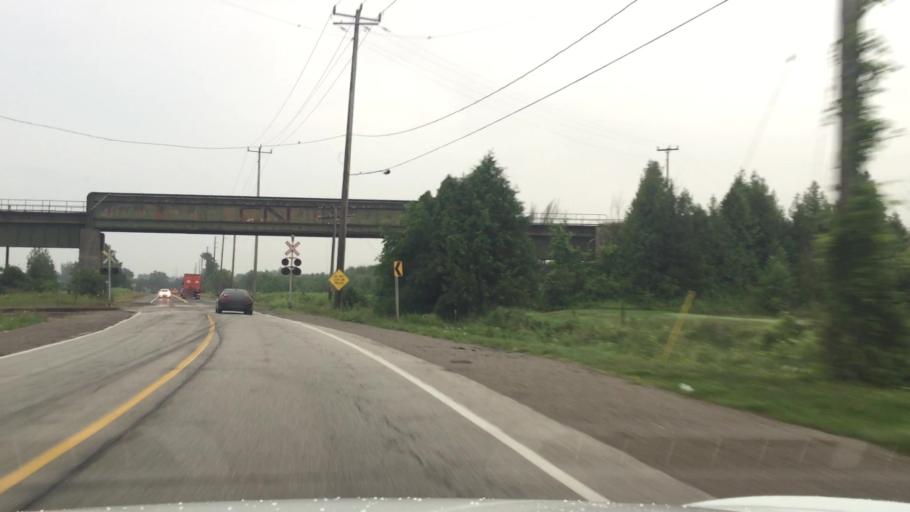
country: CA
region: Ontario
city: Markham
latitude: 43.8481
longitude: -79.2273
